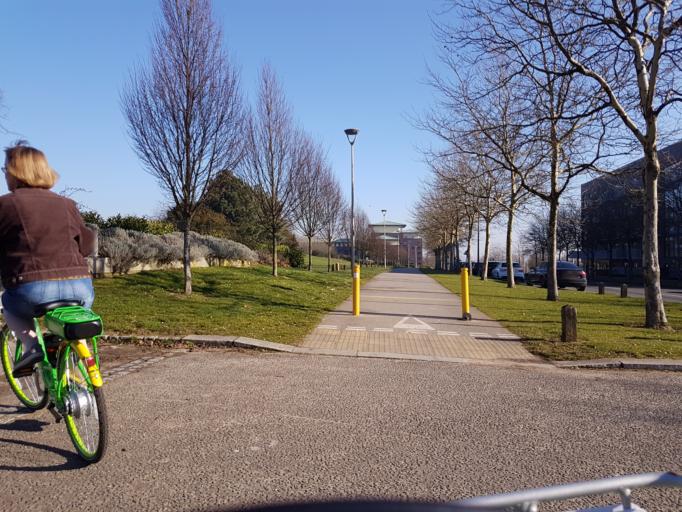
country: GB
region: England
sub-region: Milton Keynes
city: Milton Keynes
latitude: 52.0445
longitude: -0.7450
